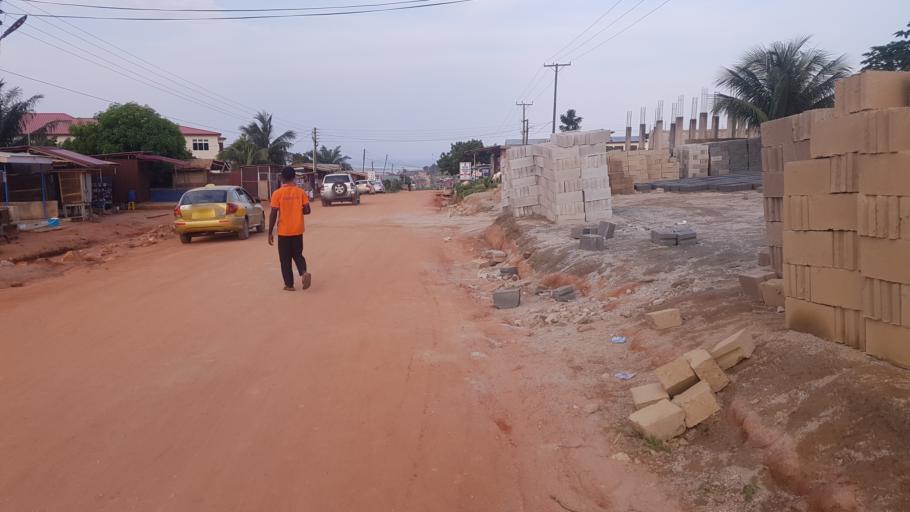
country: GH
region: Greater Accra
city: Gbawe
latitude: 5.5247
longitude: -0.3483
